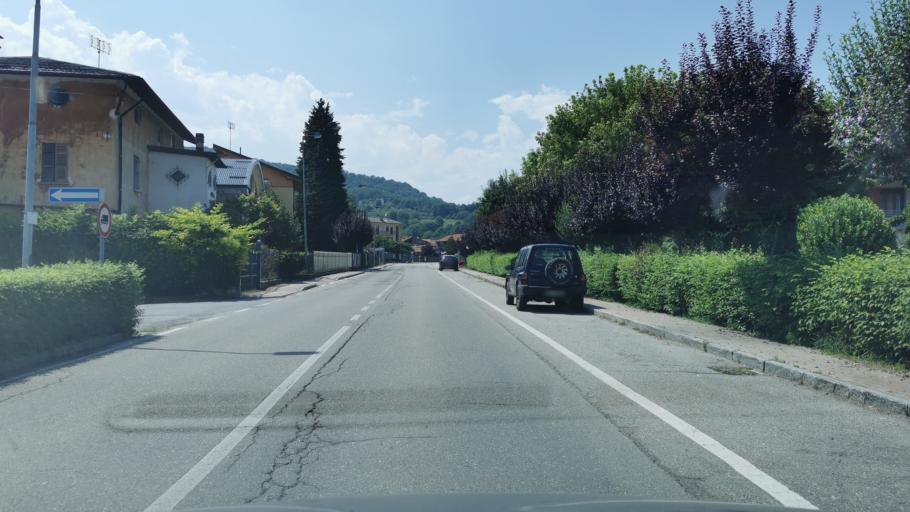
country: IT
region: Piedmont
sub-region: Provincia di Cuneo
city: Boves
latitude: 44.3315
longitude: 7.5510
